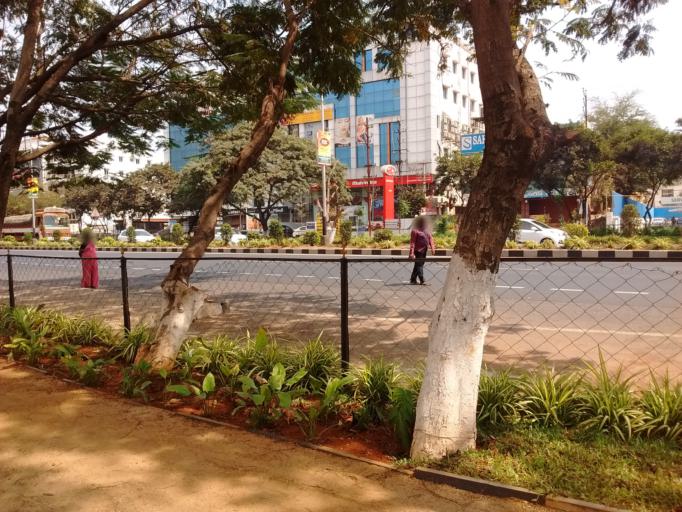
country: IN
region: Andhra Pradesh
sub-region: Krishna
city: Yanamalakuduru
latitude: 16.5138
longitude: 80.6686
